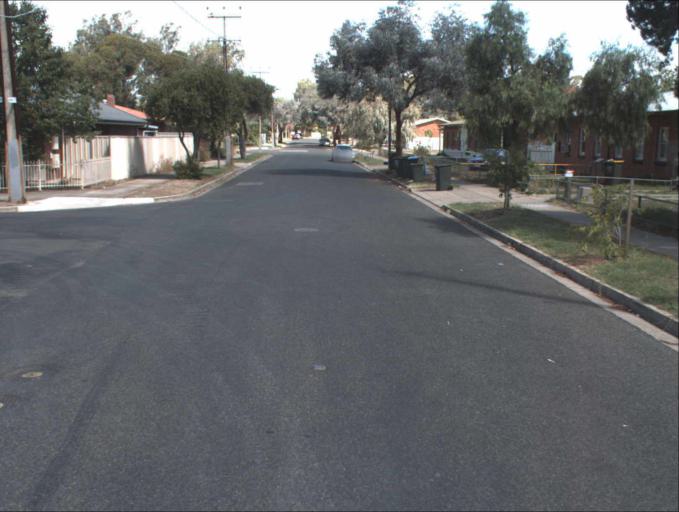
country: AU
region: South Australia
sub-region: Port Adelaide Enfield
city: Blair Athol
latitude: -34.8554
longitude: 138.5893
